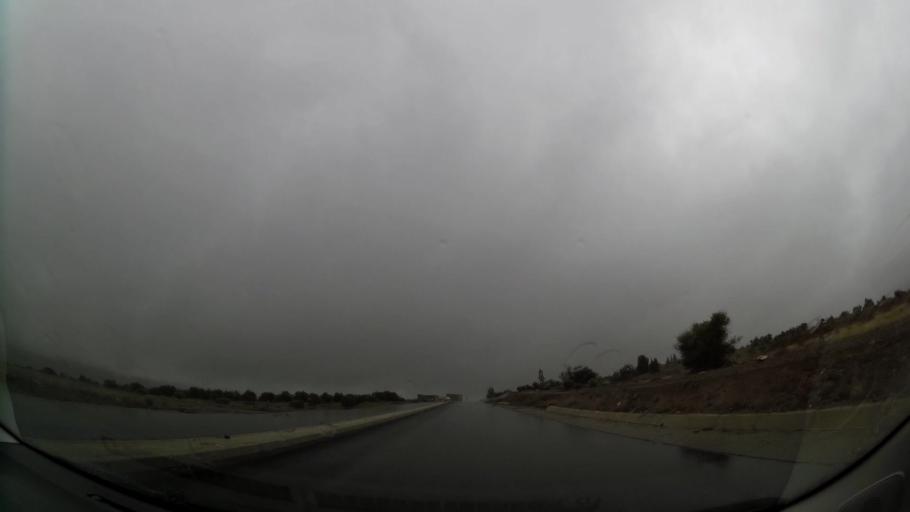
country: MA
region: Oriental
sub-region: Nador
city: Midar
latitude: 34.8625
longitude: -3.7234
